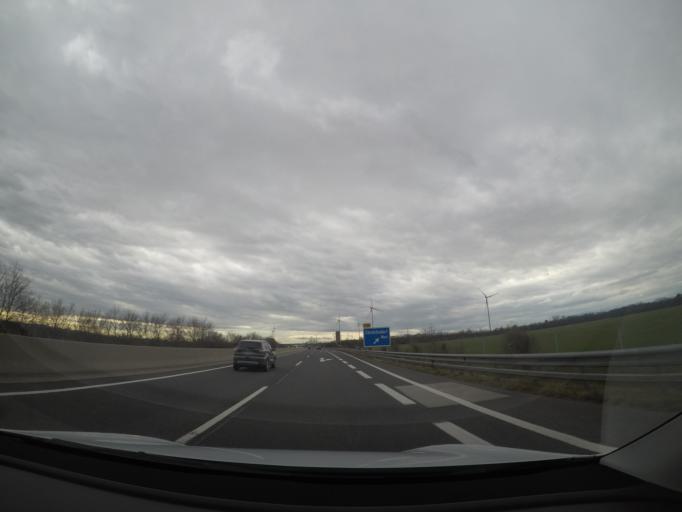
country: AT
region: Lower Austria
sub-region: Politischer Bezirk Baden
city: Trumau
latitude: 47.9683
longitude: 16.3666
